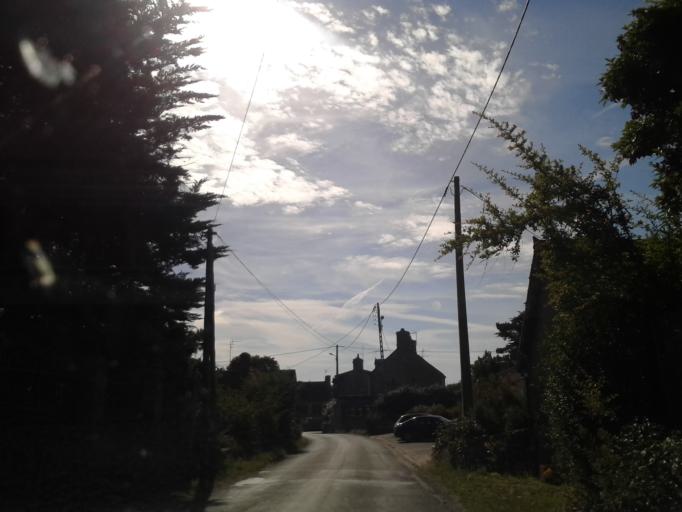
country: FR
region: Lower Normandy
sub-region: Departement de la Manche
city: Fermanville
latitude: 49.6851
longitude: -1.4572
